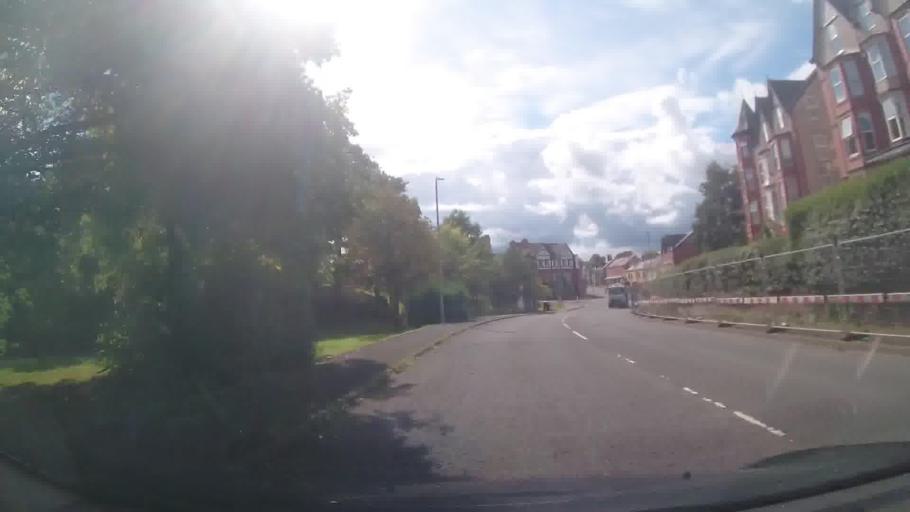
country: GB
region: Wales
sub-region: Sir Powys
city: Llandrindod Wells
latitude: 52.2354
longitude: -3.3789
